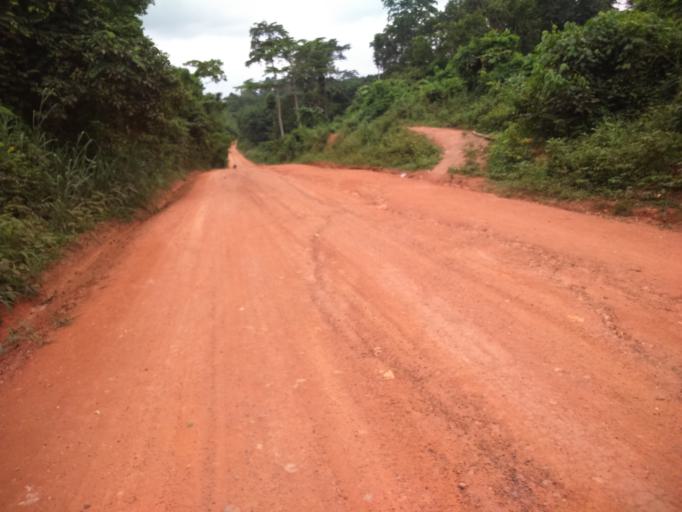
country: CI
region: Lagunes
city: Agou
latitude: 6.0831
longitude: -4.0670
